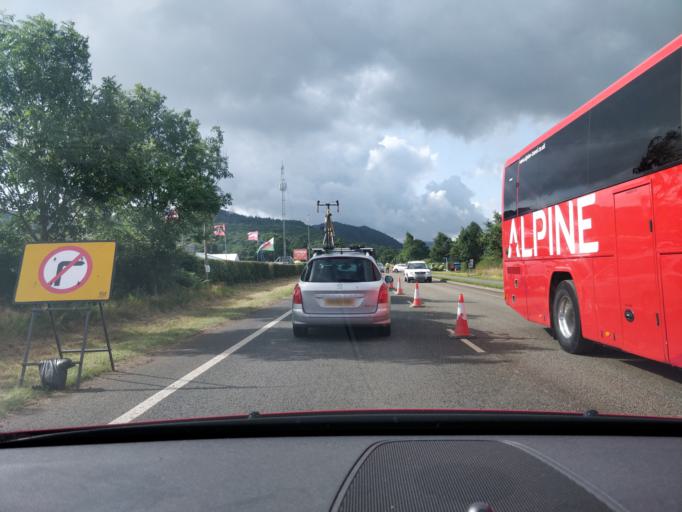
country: GB
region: Wales
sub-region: Conwy
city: Llanrwst
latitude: 53.1142
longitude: -3.7816
